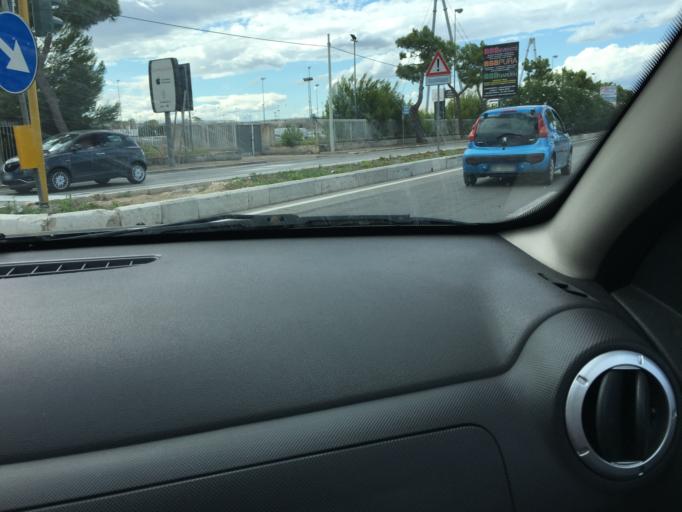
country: IT
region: Apulia
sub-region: Provincia di Bari
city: San Paolo
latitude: 41.1330
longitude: 16.8226
